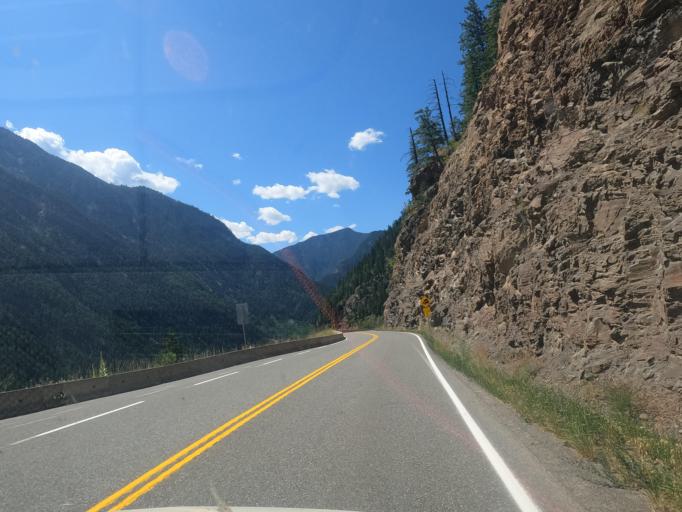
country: CA
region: British Columbia
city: Lillooet
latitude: 50.6421
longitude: -122.0267
